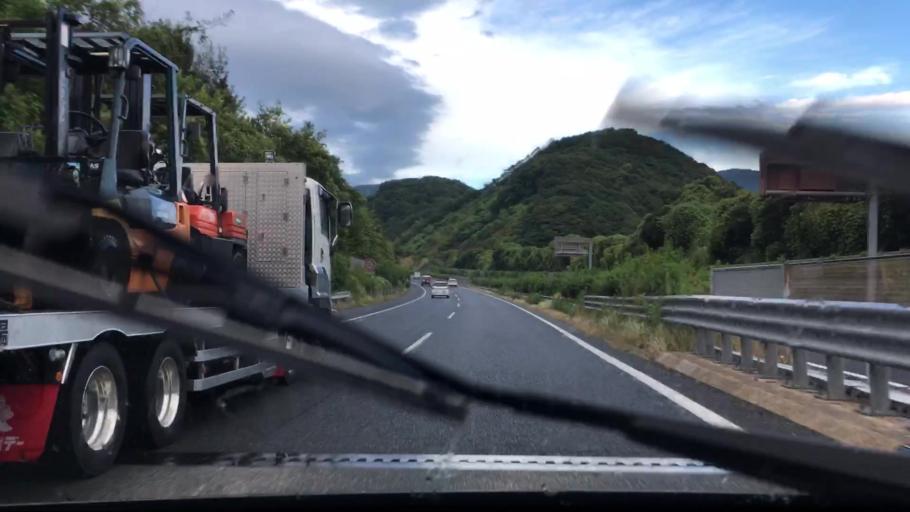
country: JP
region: Fukuoka
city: Kitakyushu
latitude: 33.8013
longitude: 130.8605
